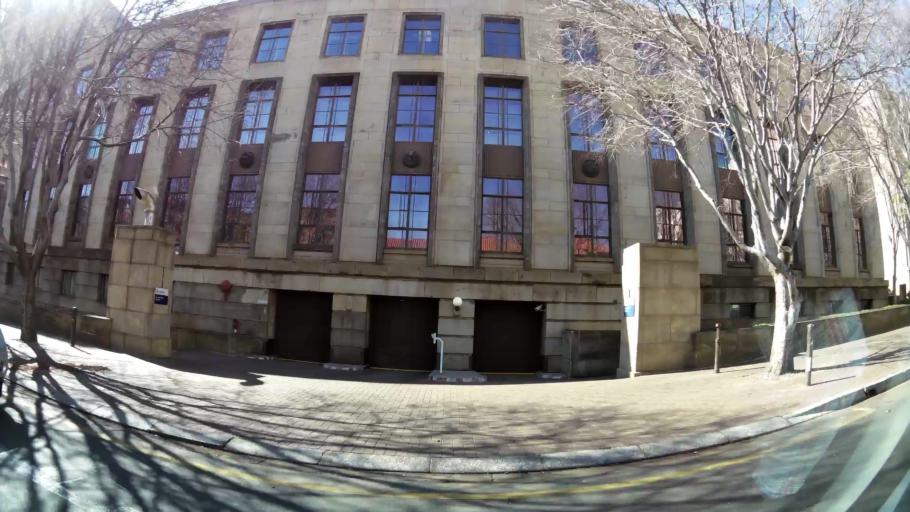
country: ZA
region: Gauteng
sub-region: City of Johannesburg Metropolitan Municipality
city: Johannesburg
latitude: -26.2080
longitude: 28.0358
